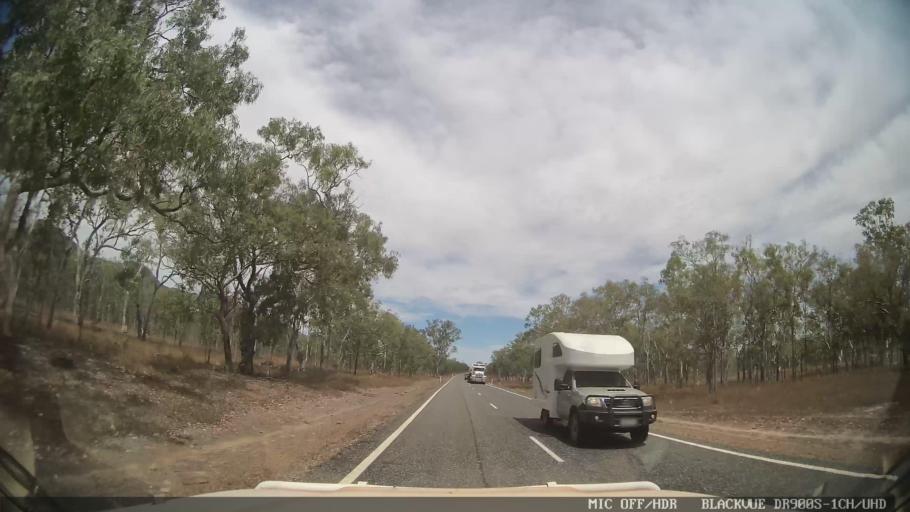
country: AU
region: Queensland
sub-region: Cairns
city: Port Douglas
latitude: -16.2407
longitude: 144.7271
